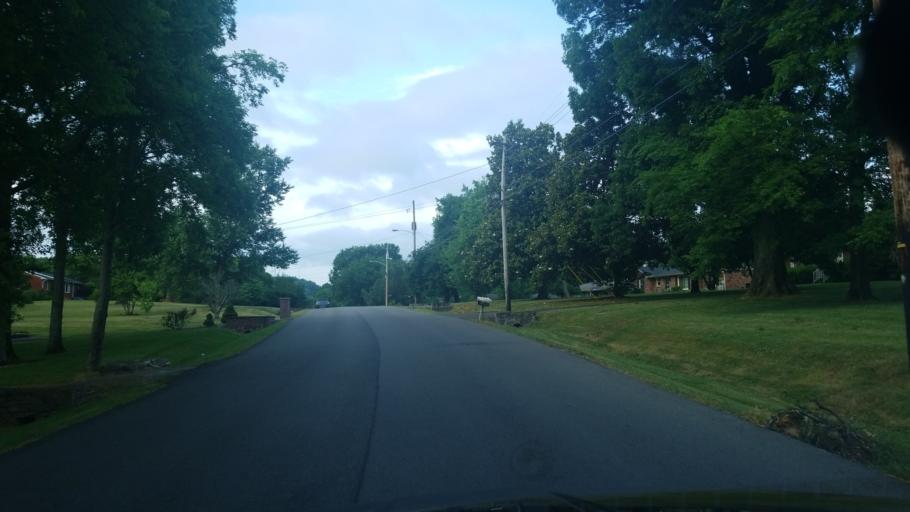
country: US
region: Tennessee
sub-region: Davidson County
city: Nashville
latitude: 36.2348
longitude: -86.7434
